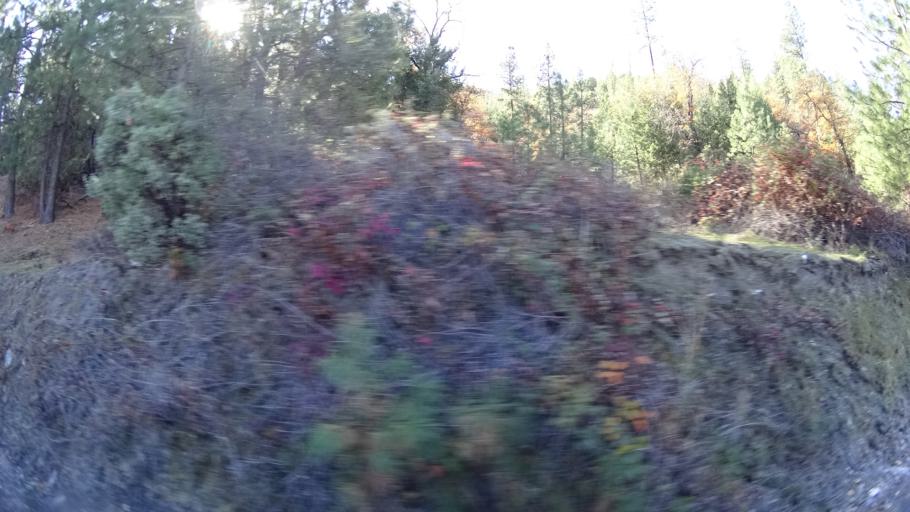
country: US
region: California
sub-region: Siskiyou County
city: Yreka
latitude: 41.8347
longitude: -122.8573
